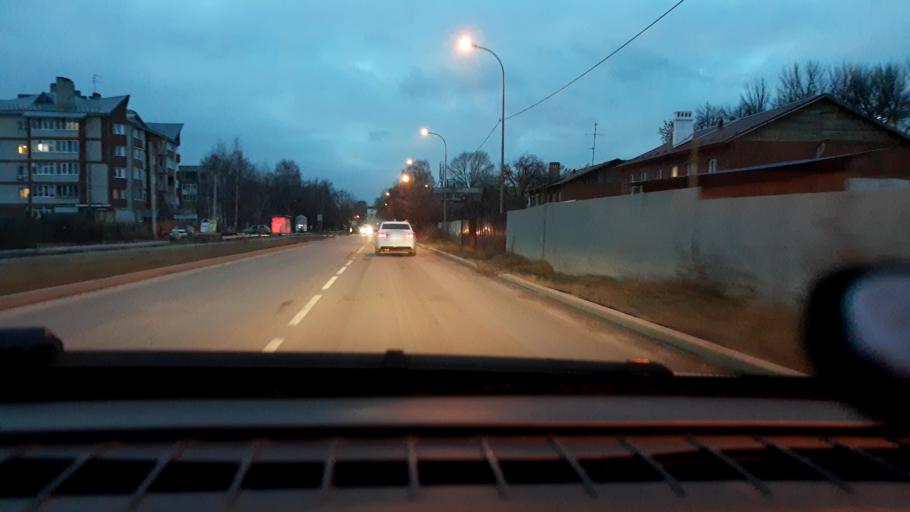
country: RU
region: Nizjnij Novgorod
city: Kstovo
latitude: 56.1393
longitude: 44.1942
